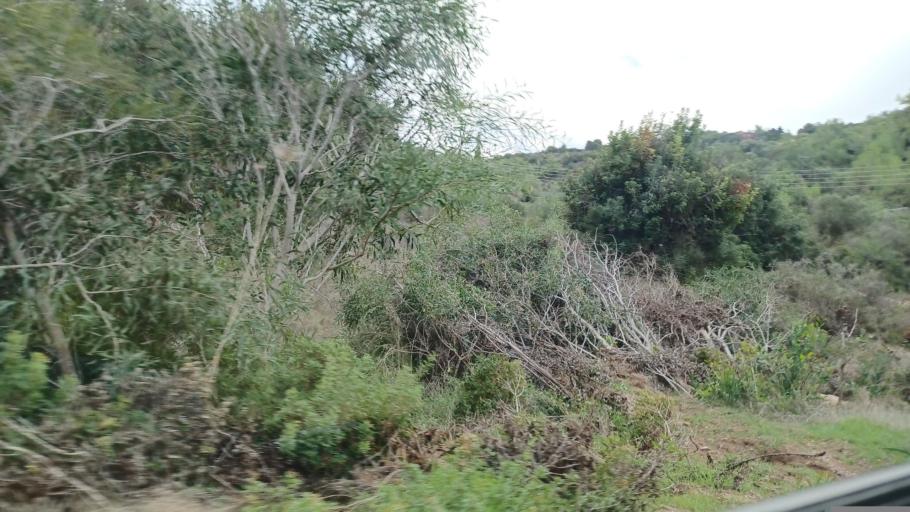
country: CY
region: Pafos
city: Polis
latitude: 35.0364
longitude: 32.3658
